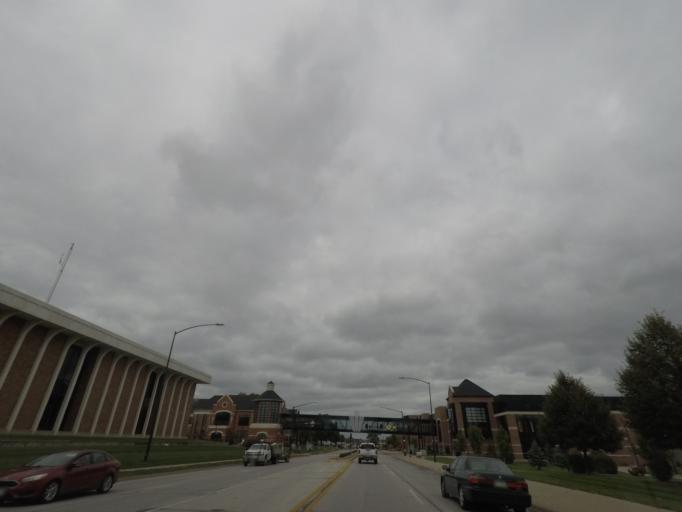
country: US
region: Iowa
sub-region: Polk County
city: Des Moines
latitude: 41.6196
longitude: -93.6005
